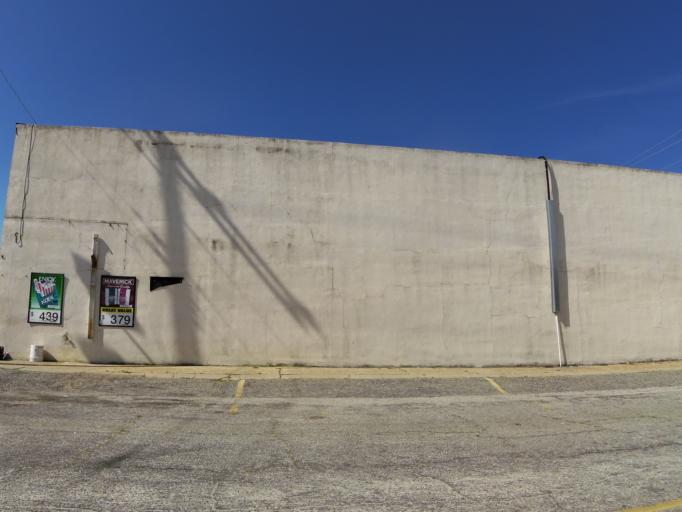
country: US
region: South Carolina
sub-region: Bamberg County
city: Denmark
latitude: 33.3243
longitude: -81.1432
